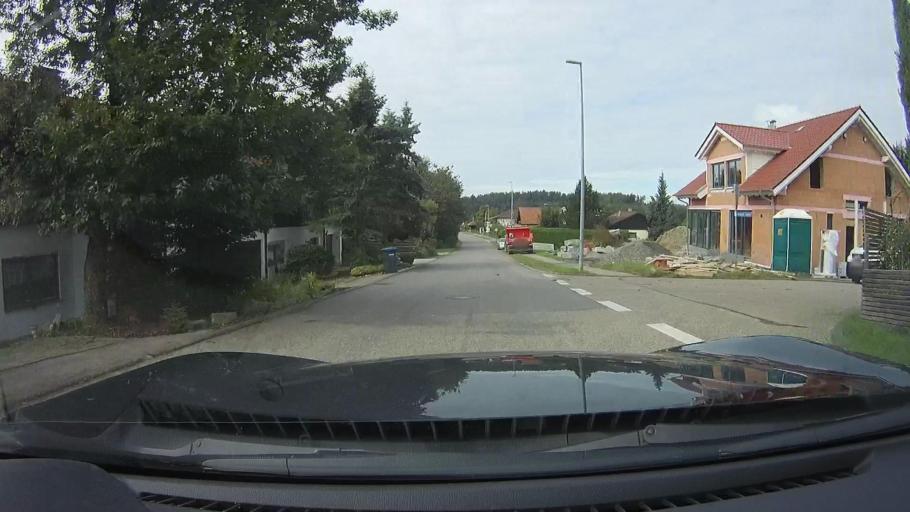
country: DE
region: Baden-Wuerttemberg
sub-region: Regierungsbezirk Stuttgart
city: Wustenrot
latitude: 49.0862
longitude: 9.4416
